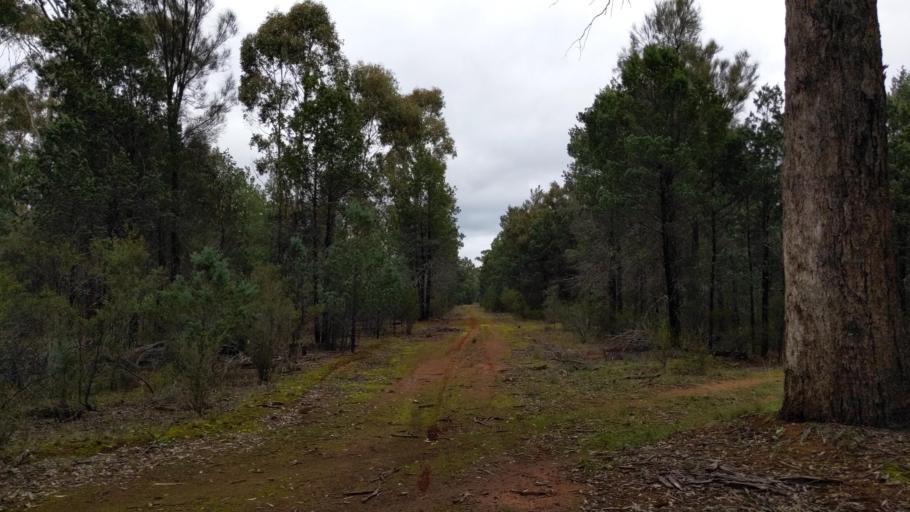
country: AU
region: New South Wales
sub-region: Coolamon
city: Coolamon
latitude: -34.8453
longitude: 146.9329
